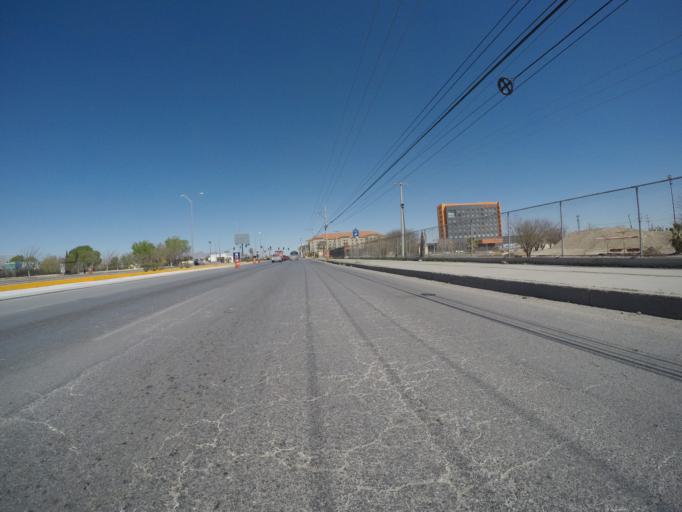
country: MX
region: Chihuahua
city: Ciudad Juarez
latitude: 31.6890
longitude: -106.4244
